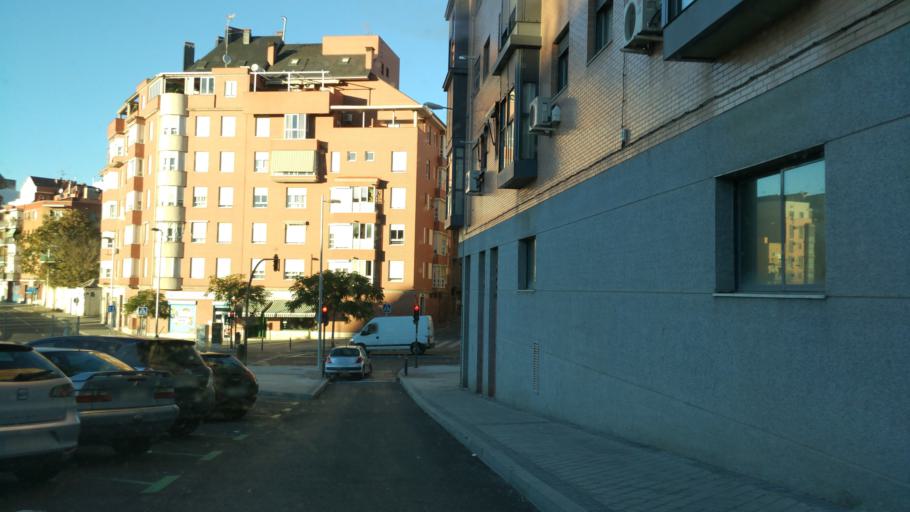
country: ES
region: Madrid
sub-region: Provincia de Madrid
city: Tetuan de las Victorias
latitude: 40.4635
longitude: -3.7052
